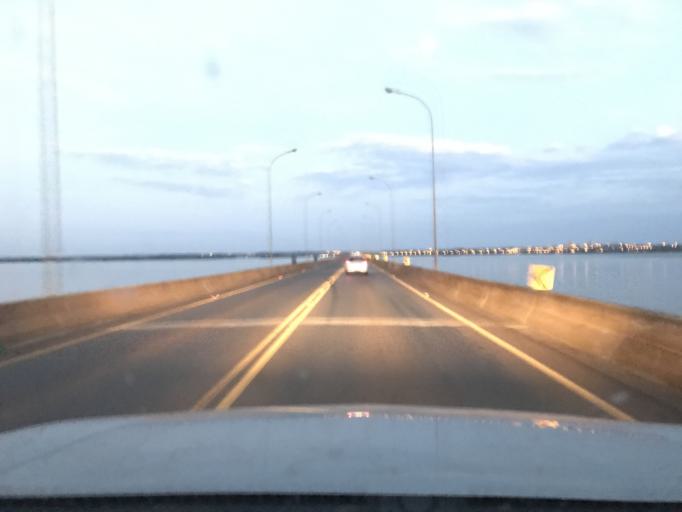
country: PY
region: Canindeyu
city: Salto del Guaira
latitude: -24.0452
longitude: -54.2714
